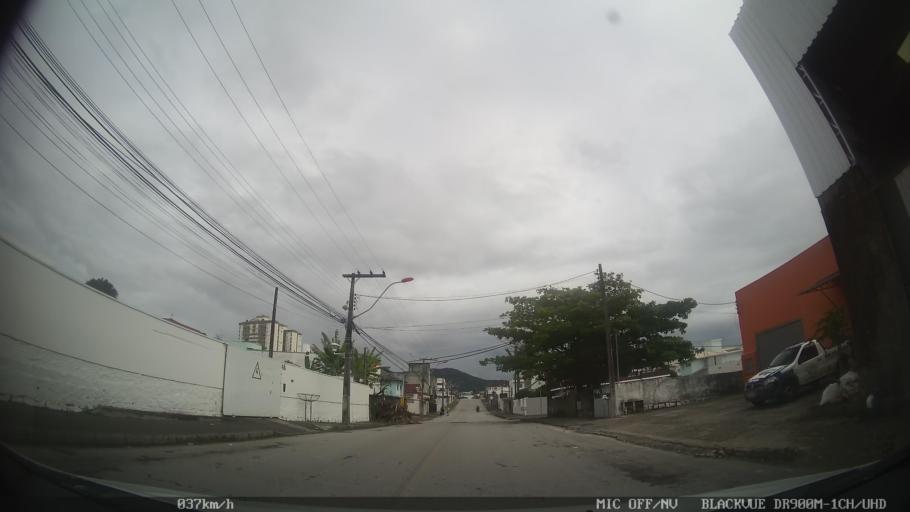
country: BR
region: Santa Catarina
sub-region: Sao Jose
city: Campinas
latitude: -27.5668
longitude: -48.6223
